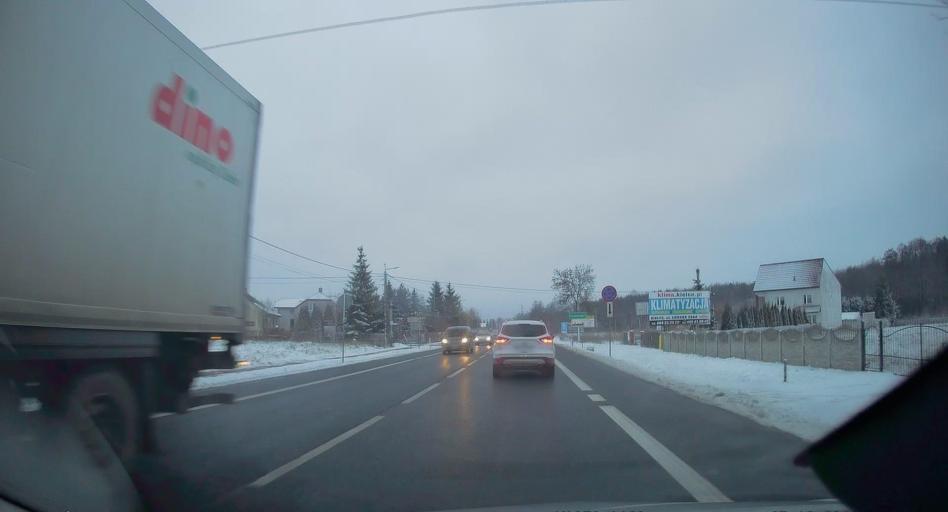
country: PL
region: Swietokrzyskie
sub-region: Powiat kielecki
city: Kostomloty Drugie
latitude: 50.9186
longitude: 20.5708
